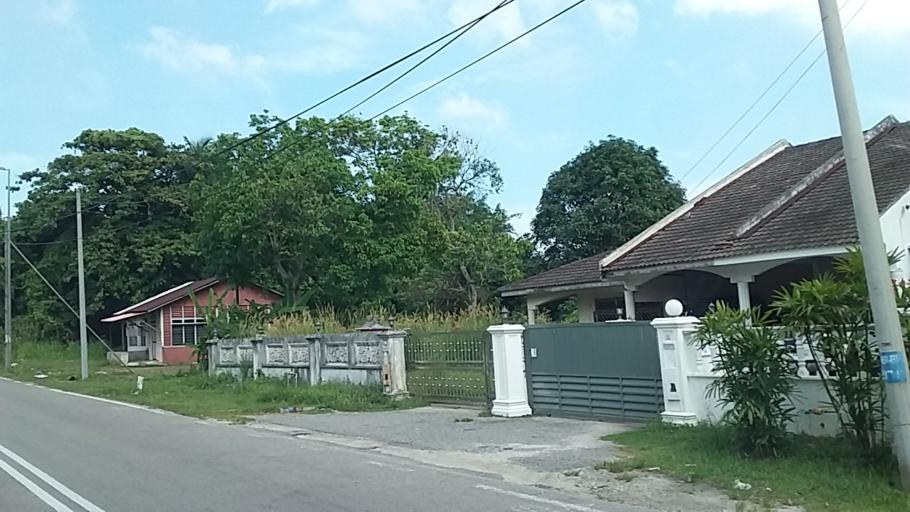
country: MY
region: Johor
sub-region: Daerah Batu Pahat
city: Batu Pahat
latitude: 1.7930
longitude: 102.8960
